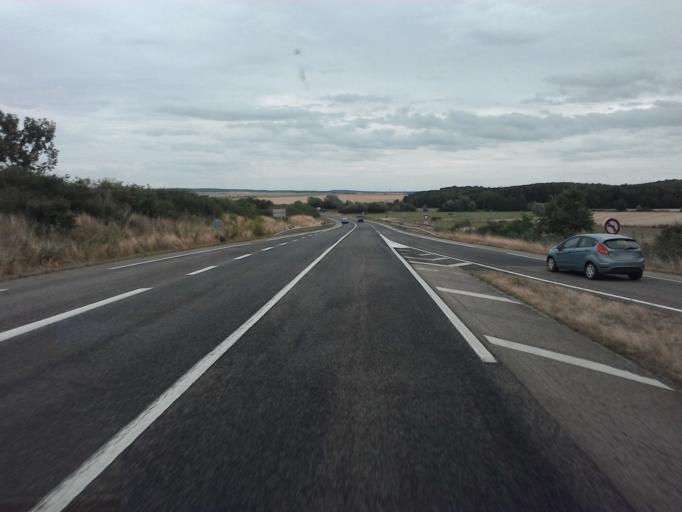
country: FR
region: Lorraine
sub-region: Departement de Meurthe-et-Moselle
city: Bainville-sur-Madon
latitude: 48.5788
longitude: 6.0538
